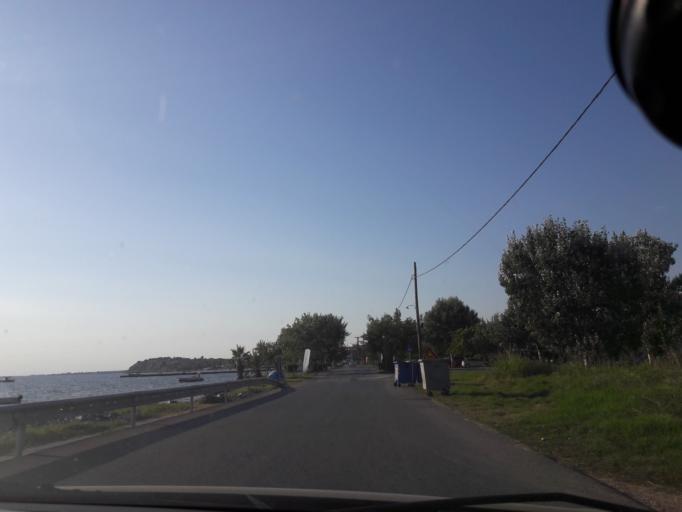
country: GR
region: Central Macedonia
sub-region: Nomos Chalkidikis
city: Nea Kallikrateia
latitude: 40.3413
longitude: 23.0164
